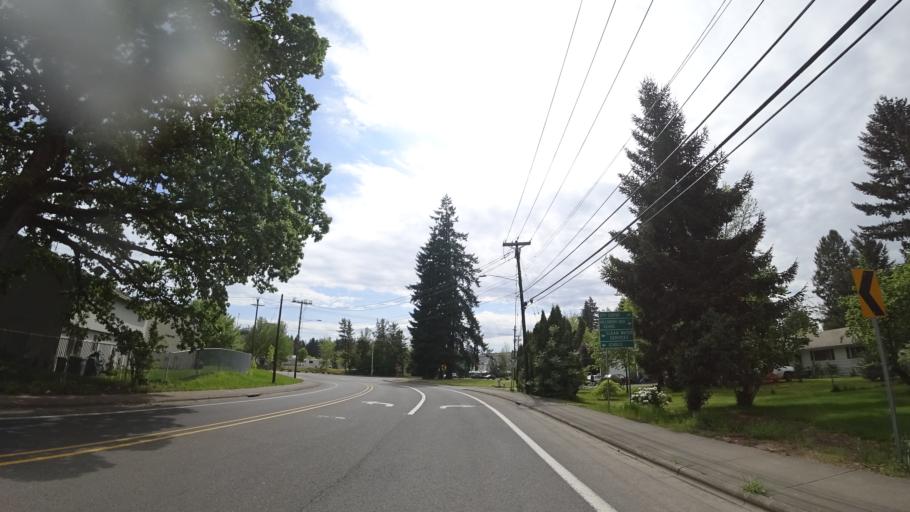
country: US
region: Oregon
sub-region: Washington County
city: Hillsboro
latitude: 45.4978
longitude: -122.9445
